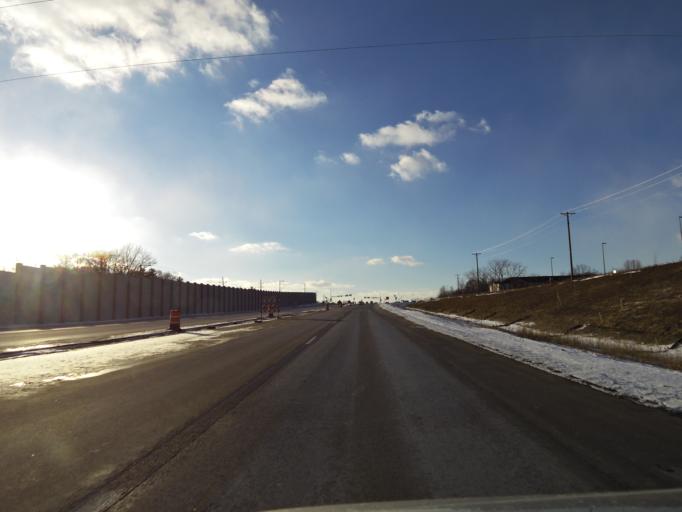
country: US
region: Minnesota
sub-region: Washington County
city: Oak Park Heights
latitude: 45.0360
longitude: -92.8022
